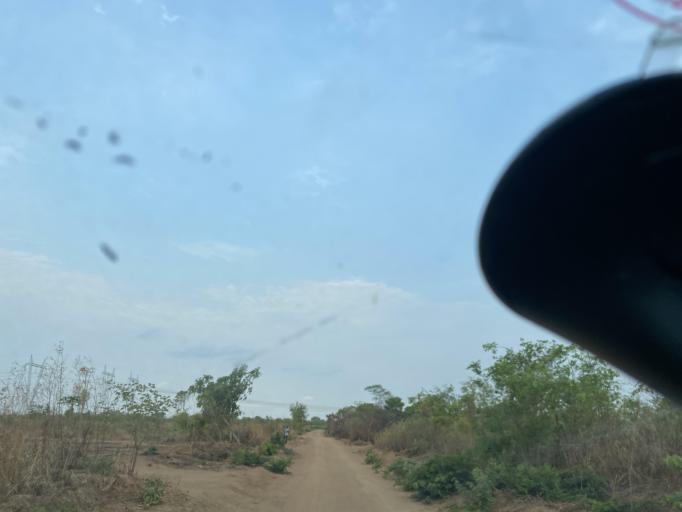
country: ZM
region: Lusaka
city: Chongwe
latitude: -15.2043
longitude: 28.5166
